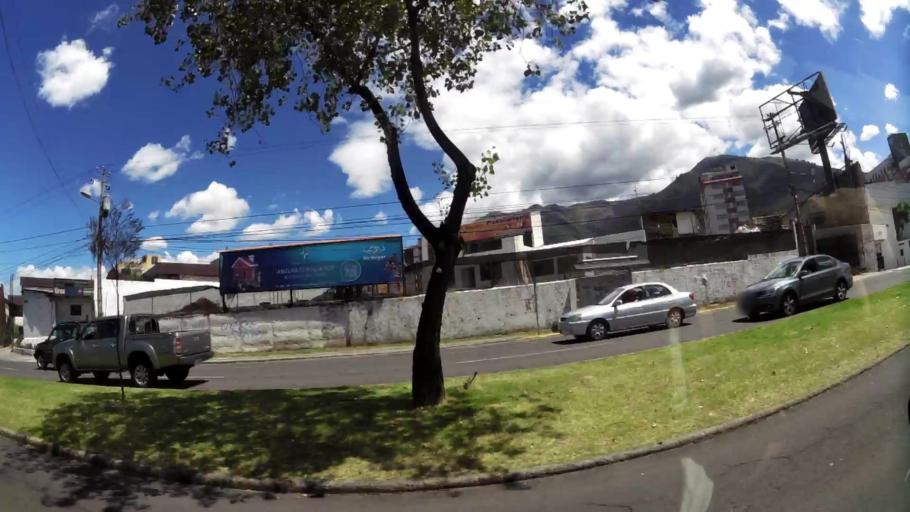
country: EC
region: Pichincha
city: Quito
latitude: -0.1757
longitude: -78.4929
